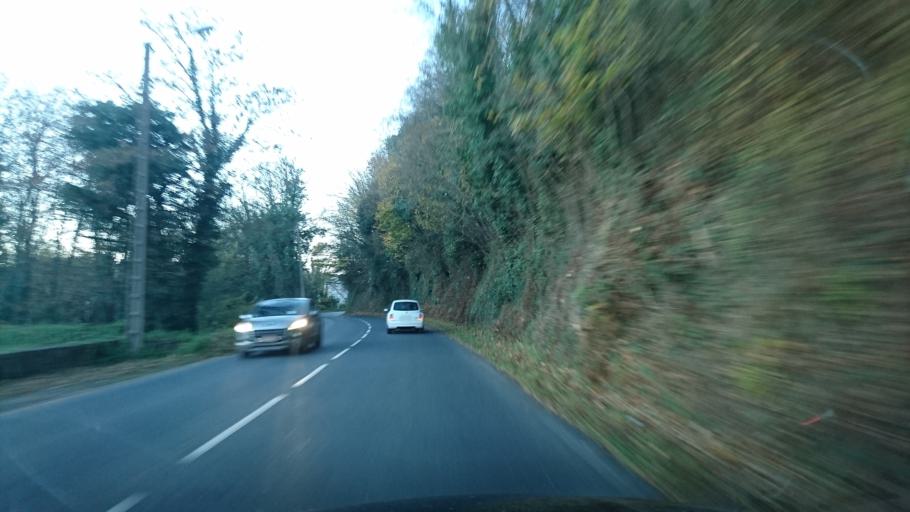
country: FR
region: Brittany
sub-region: Departement du Finistere
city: Quimperle
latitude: 47.8664
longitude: -3.5473
